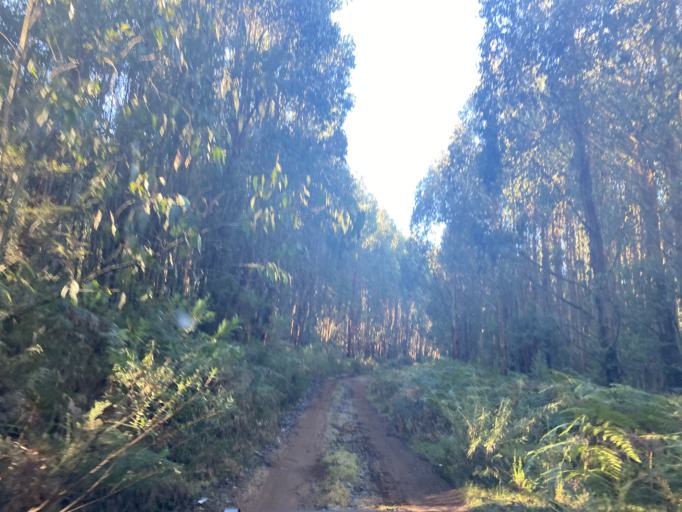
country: AU
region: Victoria
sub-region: Yarra Ranges
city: Healesville
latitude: -37.4728
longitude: 145.5776
